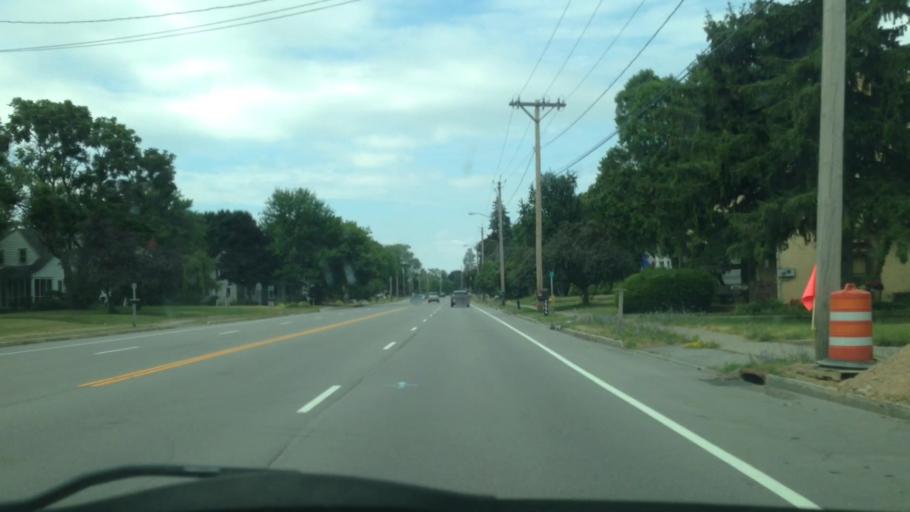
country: US
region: New York
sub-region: Monroe County
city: North Gates
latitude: 43.1367
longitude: -77.6765
